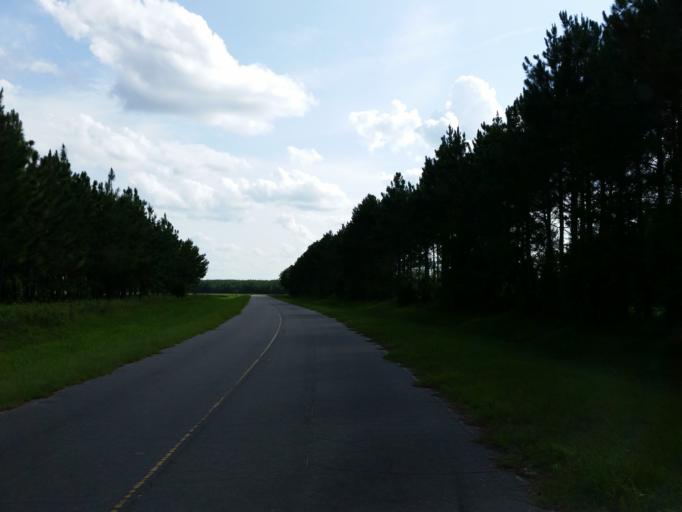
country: US
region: Georgia
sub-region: Lee County
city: Leesburg
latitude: 31.7781
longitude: -84.0279
